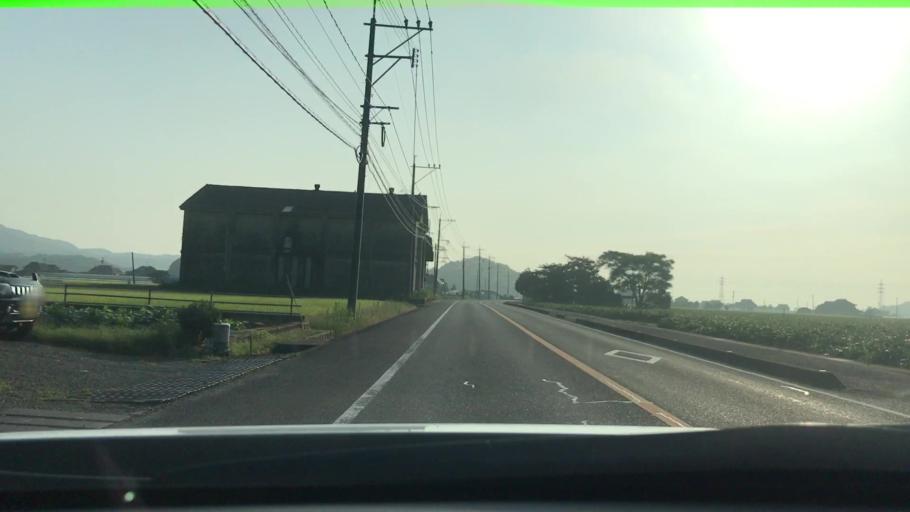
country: JP
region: Saga Prefecture
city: Takeocho-takeo
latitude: 33.2089
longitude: 130.0715
